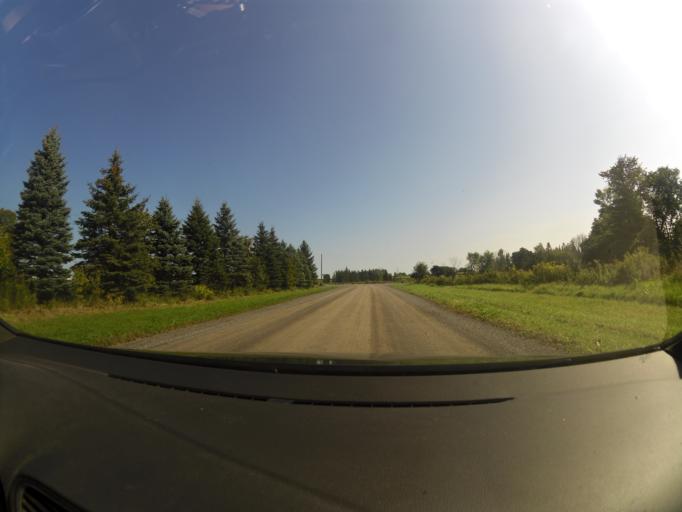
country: CA
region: Ontario
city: Arnprior
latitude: 45.3545
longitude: -76.2613
